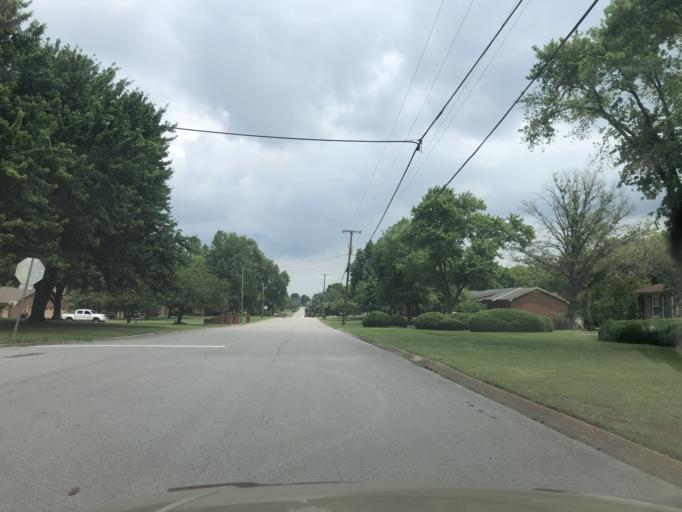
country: US
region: Tennessee
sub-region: Davidson County
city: Lakewood
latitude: 36.2348
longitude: -86.6105
